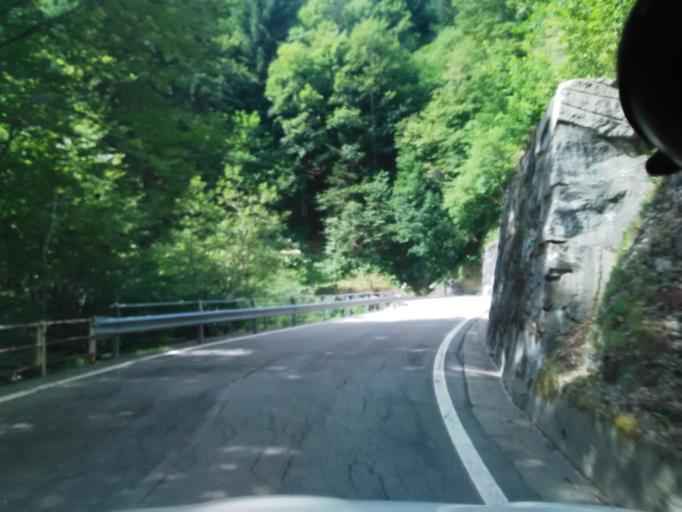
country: IT
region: Piedmont
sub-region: Provincia di Vercelli
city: Fobello
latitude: 45.8864
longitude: 8.1591
